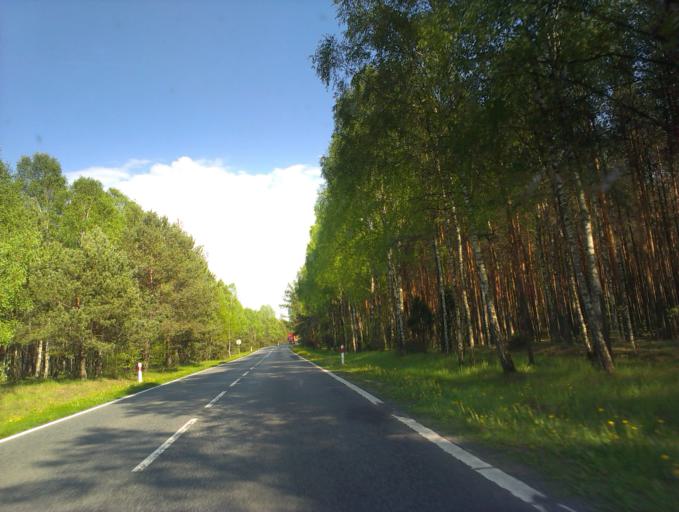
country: PL
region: Kujawsko-Pomorskie
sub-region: Powiat tucholski
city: Lubiewo
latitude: 53.4945
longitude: 18.0781
